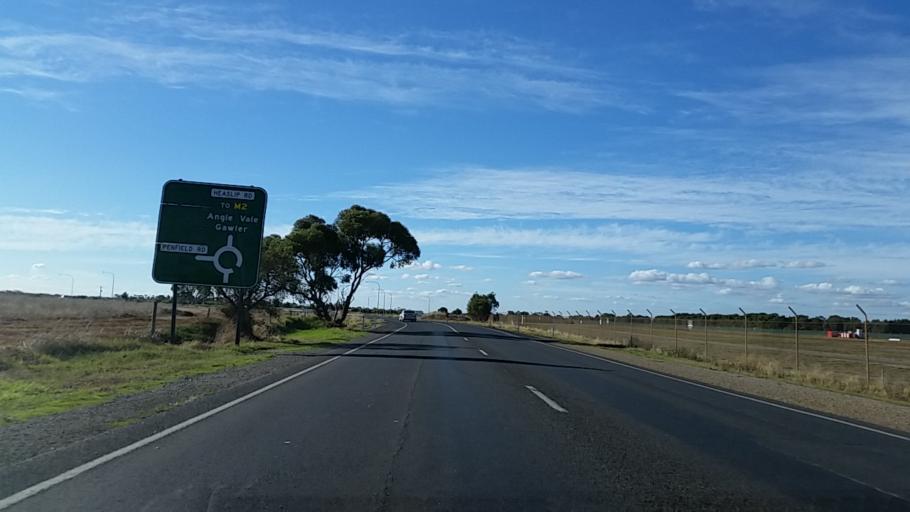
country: AU
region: South Australia
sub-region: Playford
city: Virginia
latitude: -34.6953
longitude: 138.6141
